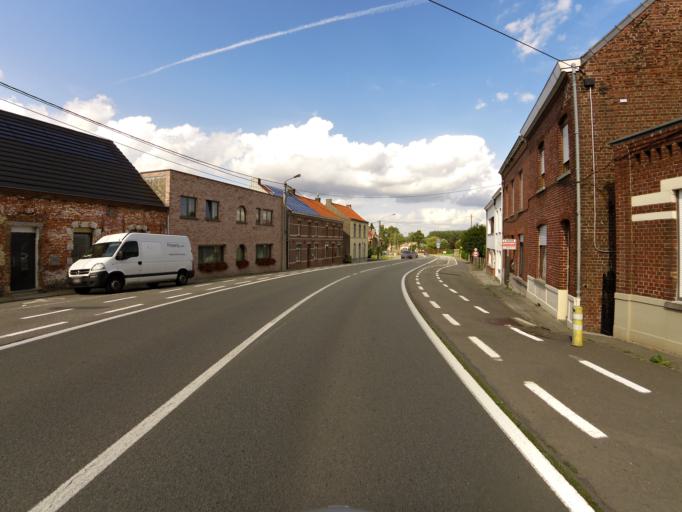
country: BE
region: Flanders
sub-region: Provincie Oost-Vlaanderen
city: Ronse
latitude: 50.7152
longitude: 3.5792
